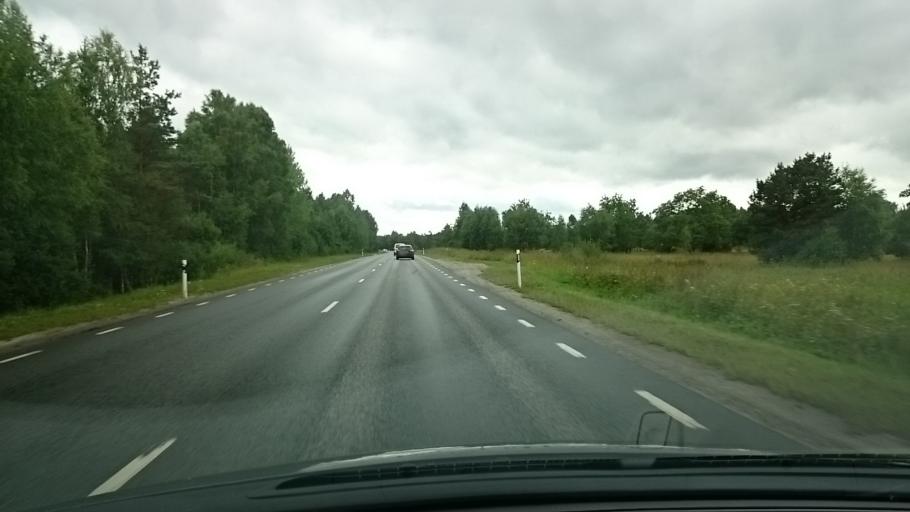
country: EE
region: Harju
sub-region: Keila linn
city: Keila
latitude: 59.2774
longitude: 24.3027
